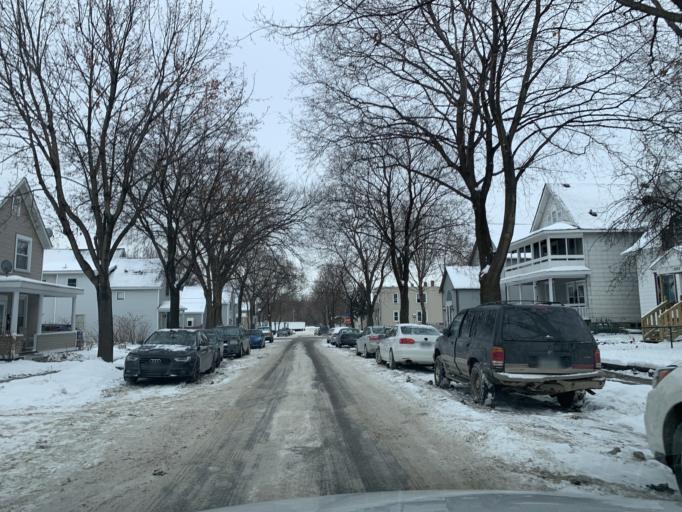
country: US
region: Minnesota
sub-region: Hennepin County
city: Minneapolis
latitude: 44.9797
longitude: -93.2982
